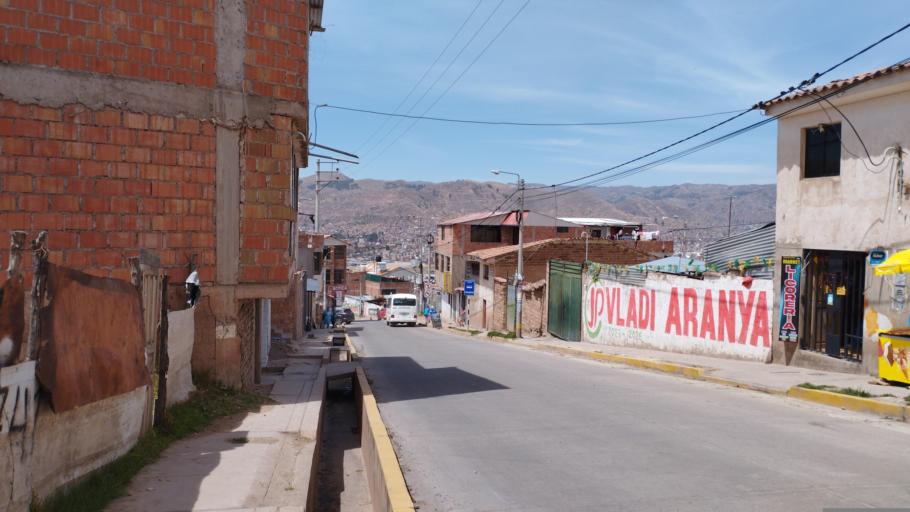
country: PE
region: Cusco
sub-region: Provincia de Cusco
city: Cusco
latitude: -13.5249
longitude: -71.9289
